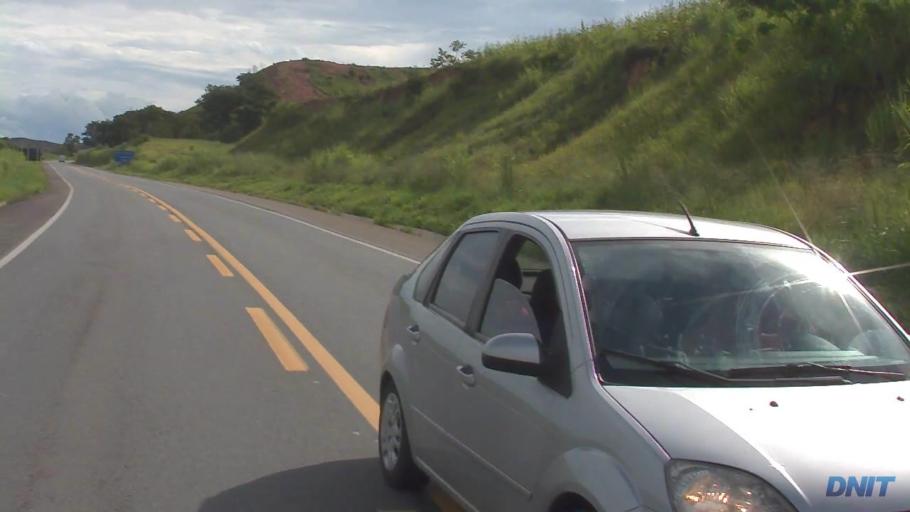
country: BR
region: Minas Gerais
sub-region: Belo Oriente
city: Belo Oriente
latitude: -19.1907
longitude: -42.2731
